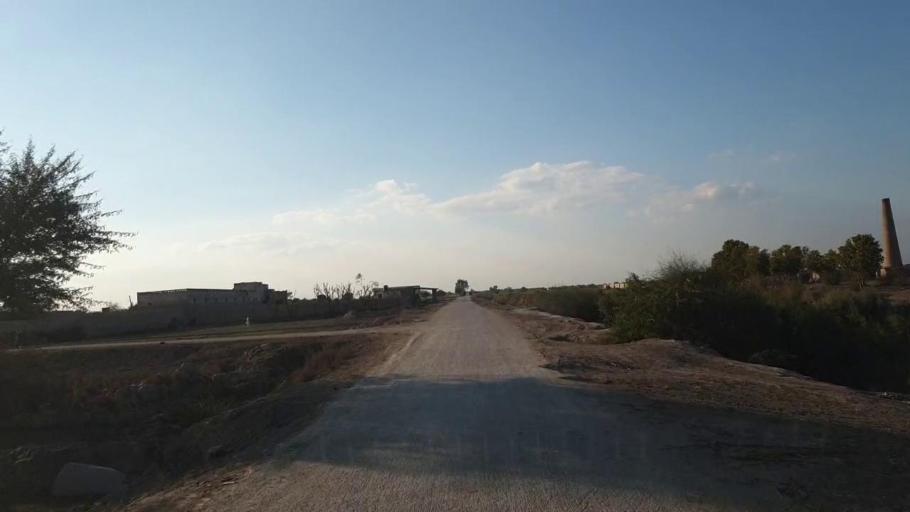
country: PK
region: Sindh
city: Shahpur Chakar
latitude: 26.1459
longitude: 68.5361
